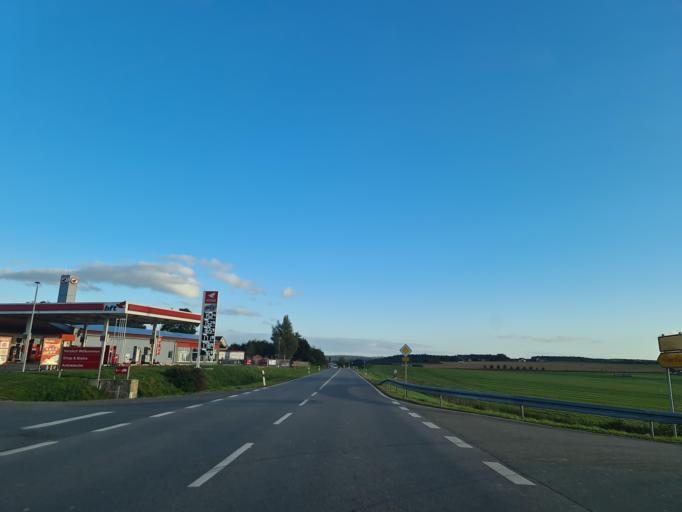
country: DE
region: Thuringia
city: Wildetaube
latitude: 50.7176
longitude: 12.1111
